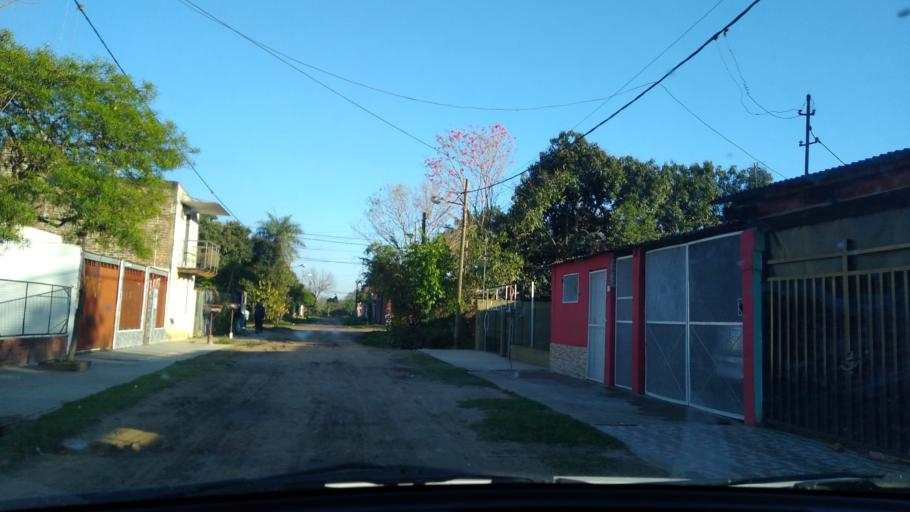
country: AR
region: Chaco
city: Resistencia
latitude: -27.4849
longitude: -58.9710
